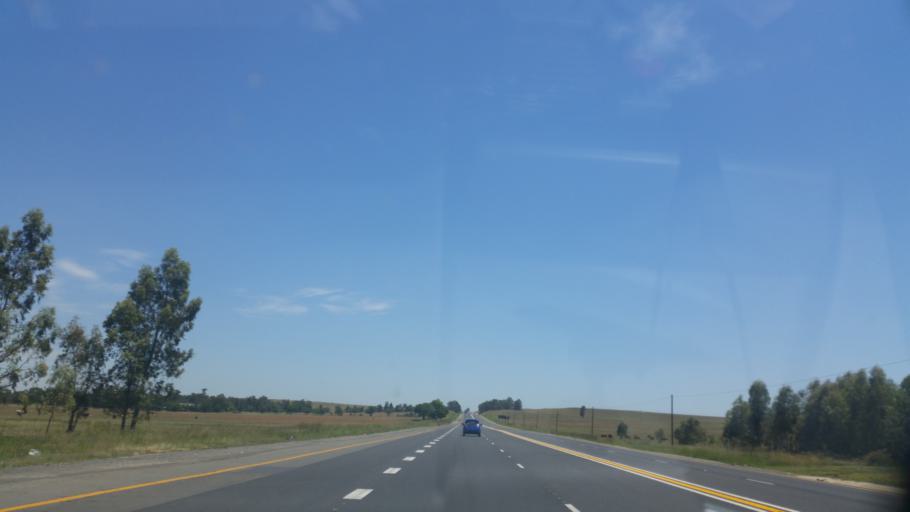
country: ZA
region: Orange Free State
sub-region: Thabo Mofutsanyana District Municipality
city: Harrismith
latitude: -28.1655
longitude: 29.0744
